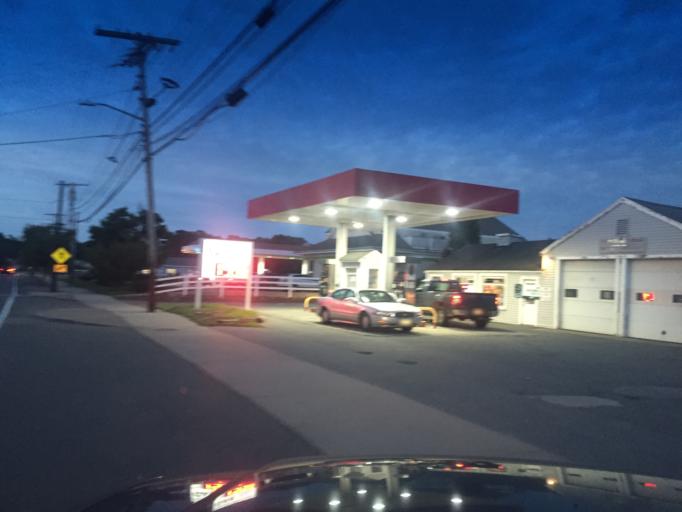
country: US
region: Massachusetts
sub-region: Barnstable County
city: Buzzards Bay
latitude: 41.7463
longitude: -70.6103
